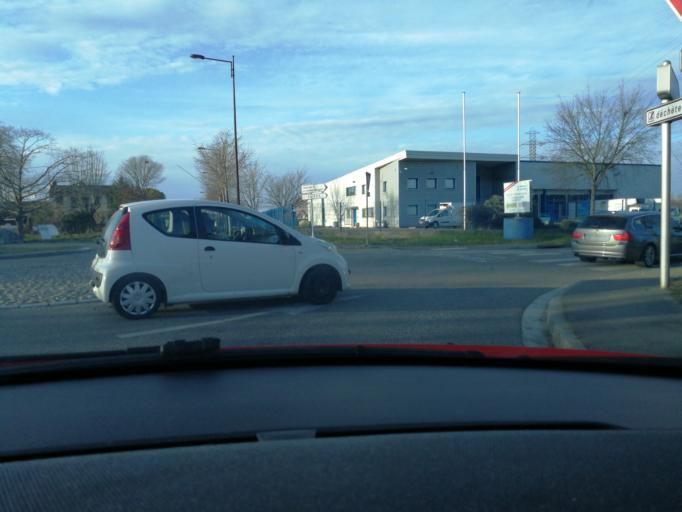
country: FR
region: Midi-Pyrenees
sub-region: Departement de la Haute-Garonne
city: Blagnac
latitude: 43.6315
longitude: 1.4158
